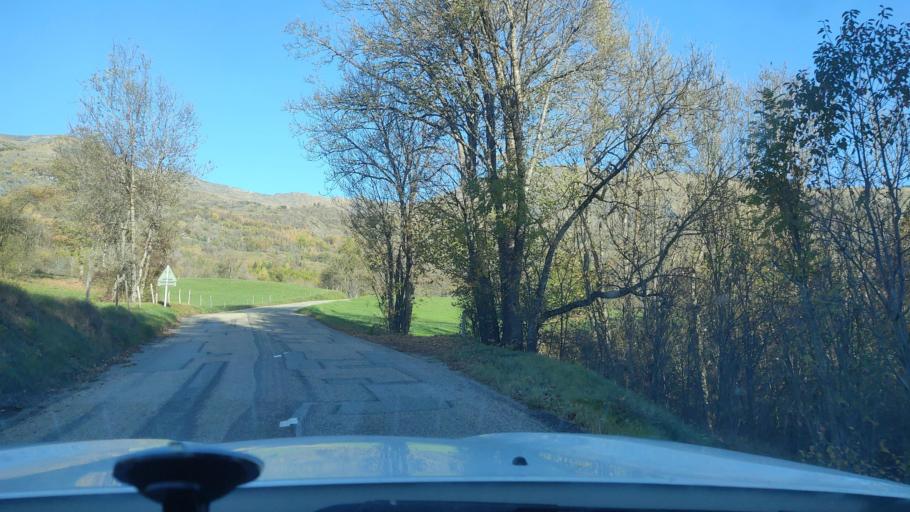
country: FR
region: Rhone-Alpes
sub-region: Departement de la Savoie
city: Saint-Jean-de-Maurienne
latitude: 45.2689
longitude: 6.3105
